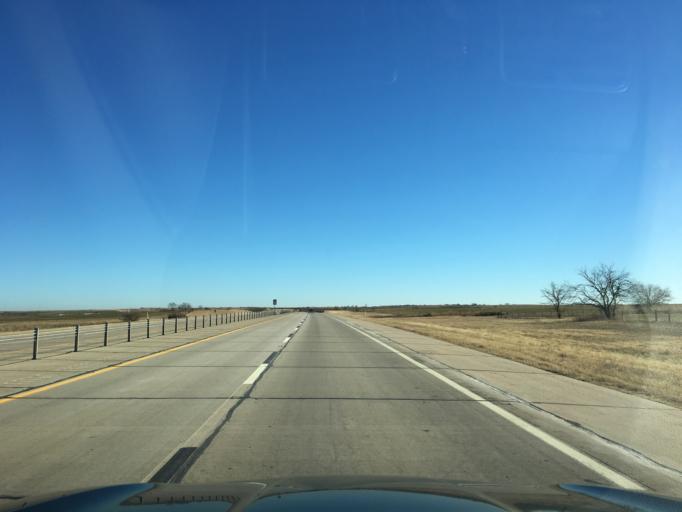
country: US
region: Oklahoma
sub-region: Noble County
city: Perry
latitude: 36.3995
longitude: -97.2407
